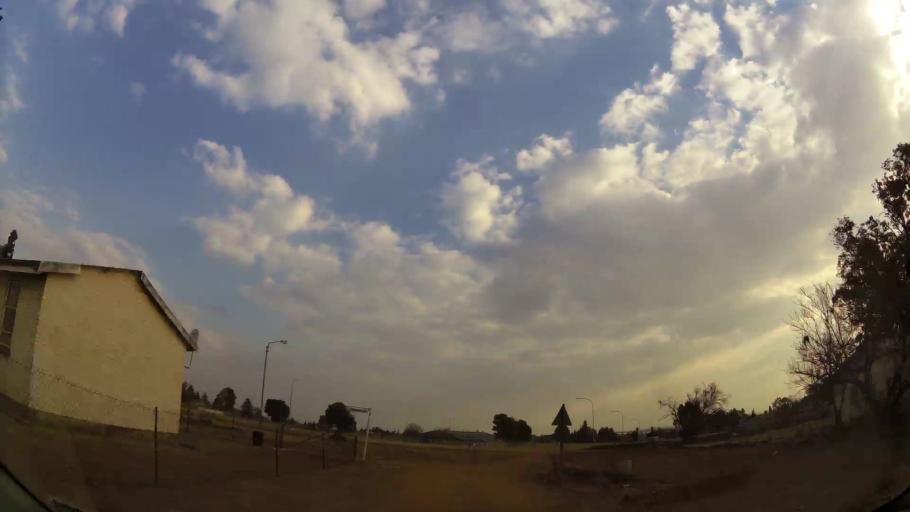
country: ZA
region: Gauteng
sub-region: Ekurhuleni Metropolitan Municipality
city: Benoni
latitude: -26.1592
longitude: 28.3030
